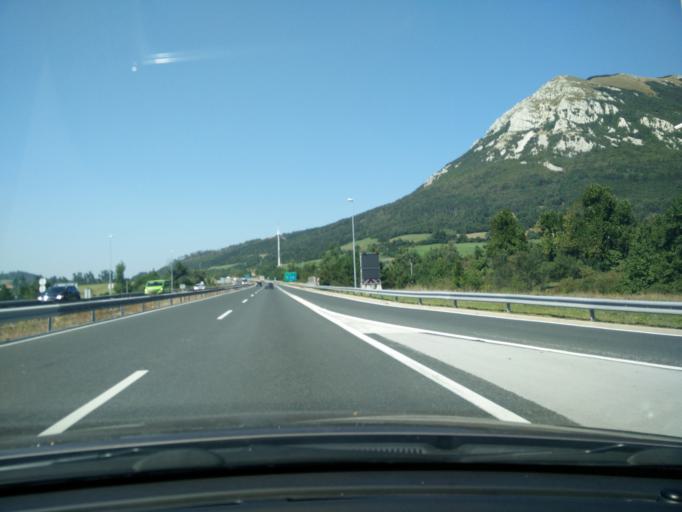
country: SI
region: Divaca
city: Divaca
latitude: 45.7594
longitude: 14.0757
